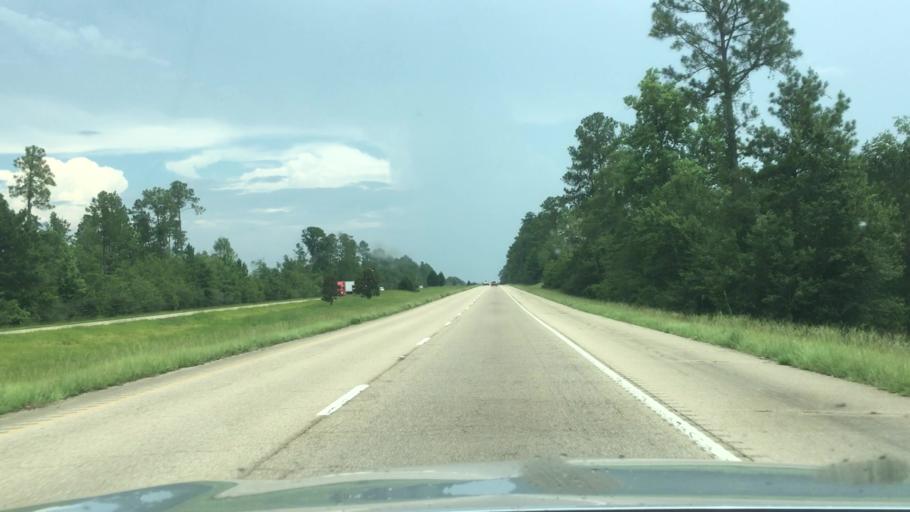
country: US
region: Mississippi
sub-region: Lamar County
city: Lumberton
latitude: 30.9713
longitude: -89.4335
